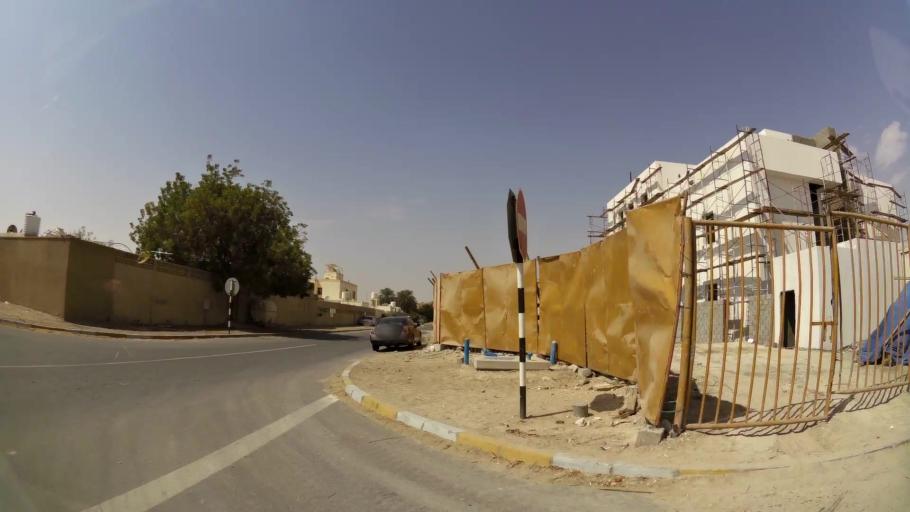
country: AE
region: Abu Dhabi
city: Abu Dhabi
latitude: 24.2866
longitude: 54.6518
